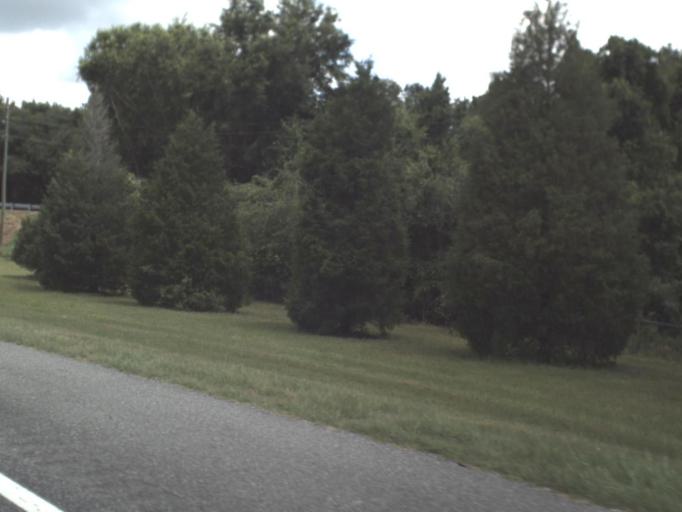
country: US
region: Florida
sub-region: Columbia County
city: Five Points
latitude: 30.2208
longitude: -82.7115
